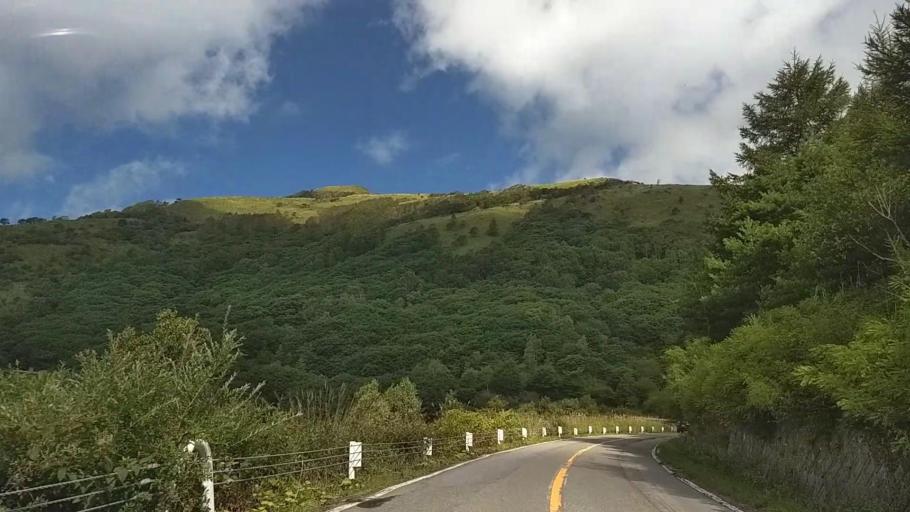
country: JP
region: Nagano
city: Suwa
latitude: 36.0962
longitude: 138.2073
